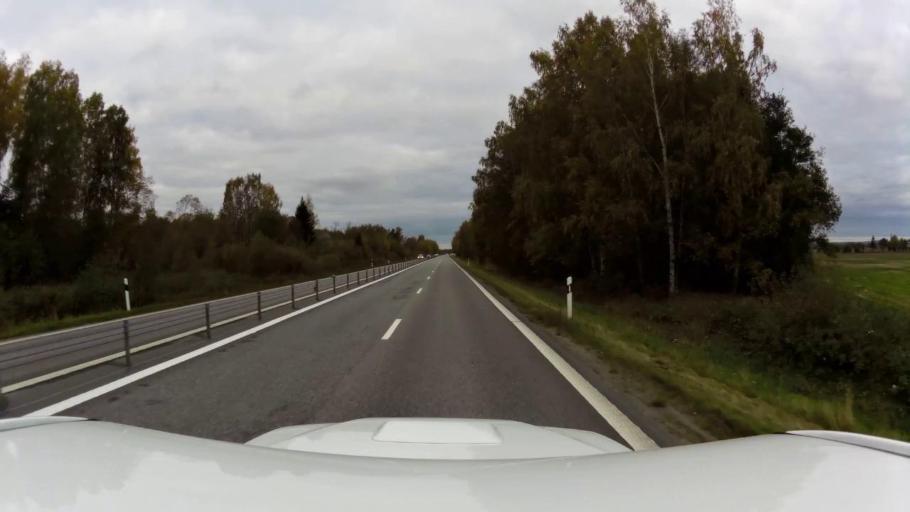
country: SE
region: OEstergoetland
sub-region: Linkopings Kommun
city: Malmslatt
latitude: 58.4408
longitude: 15.5218
